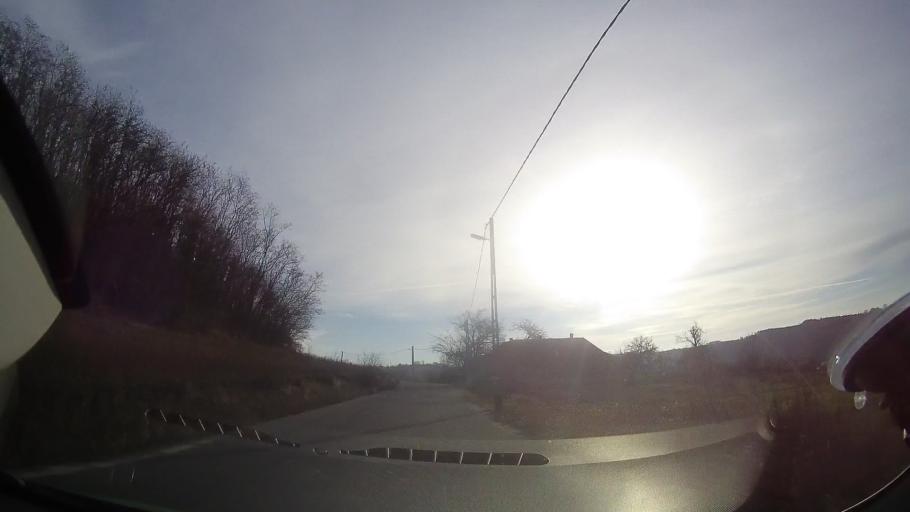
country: RO
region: Bihor
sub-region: Comuna Sarbi
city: Burzuc
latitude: 47.1352
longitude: 22.1857
